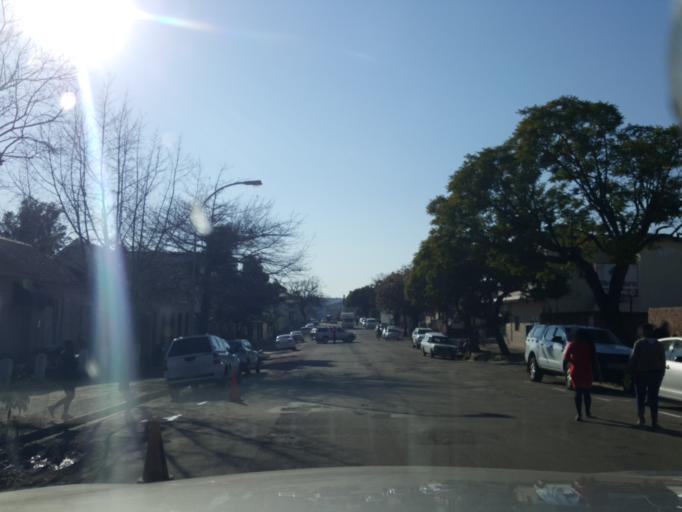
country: ZA
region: Eastern Cape
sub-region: Cacadu District Municipality
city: Grahamstown
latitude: -33.3098
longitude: 26.5237
